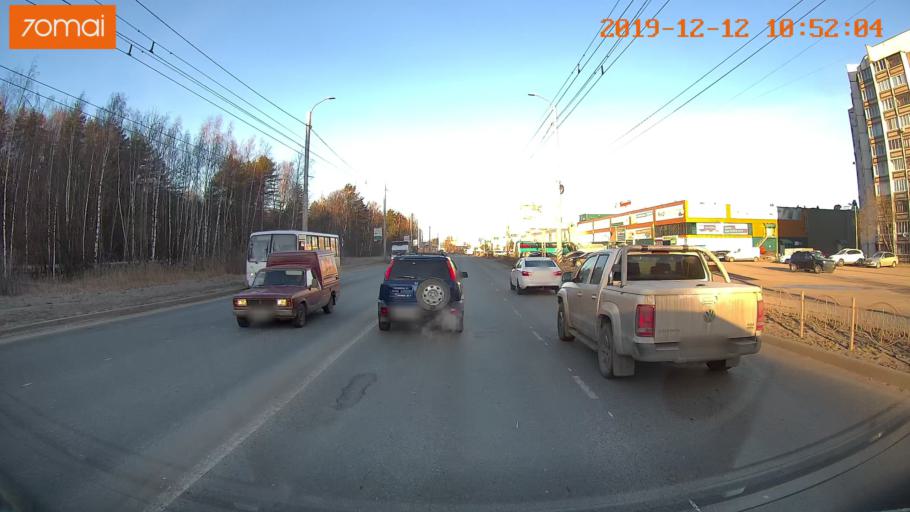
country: RU
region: Ivanovo
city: Kokhma
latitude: 56.9546
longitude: 41.0420
